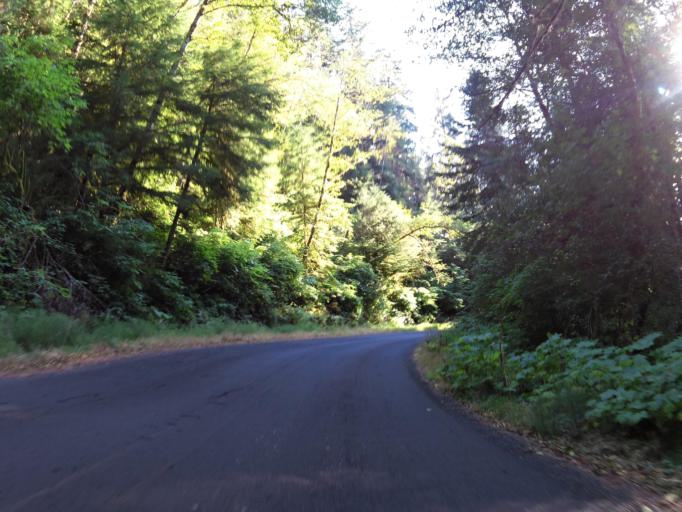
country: US
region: Oregon
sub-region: Lincoln County
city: Rose Lodge
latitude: 45.0389
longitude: -123.9110
